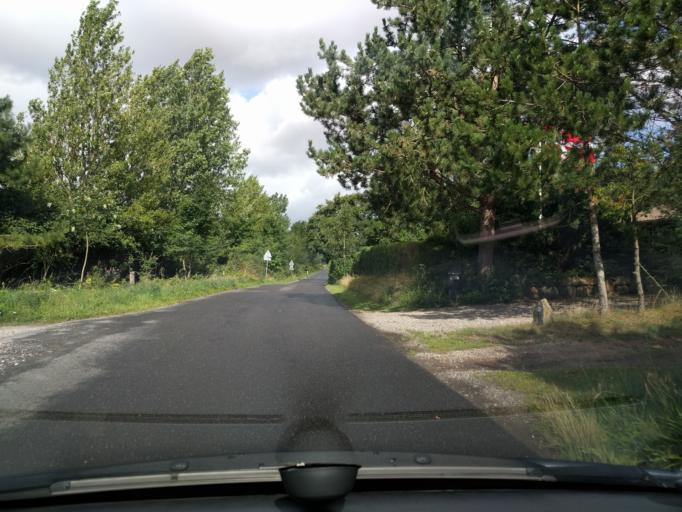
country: DK
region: South Denmark
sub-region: Kerteminde Kommune
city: Langeskov
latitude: 55.3750
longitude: 10.5846
